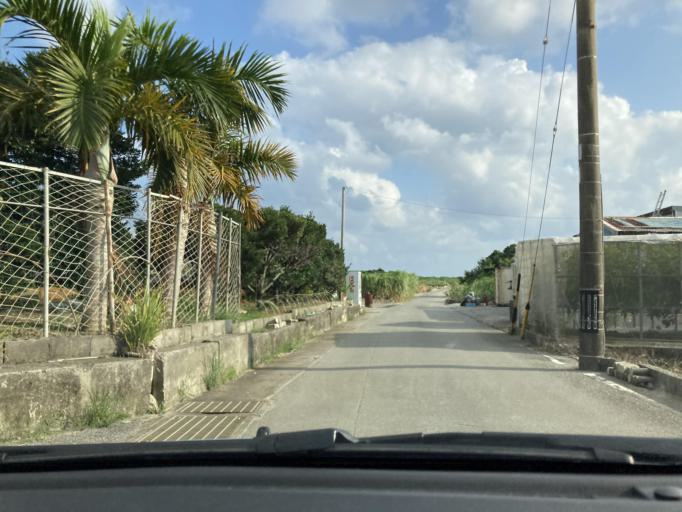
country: JP
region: Okinawa
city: Itoman
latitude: 26.0856
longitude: 127.6627
